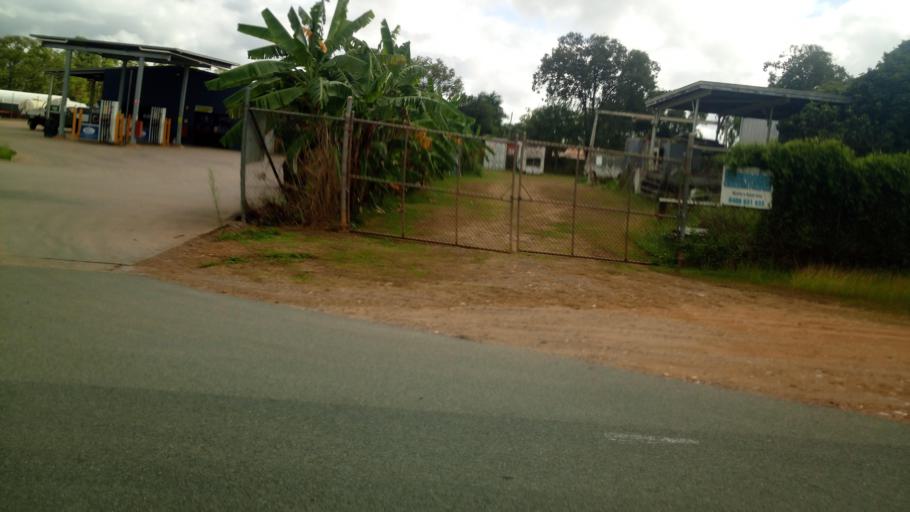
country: AU
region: Queensland
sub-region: Tablelands
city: Mareeba
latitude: -16.9737
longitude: 145.4133
